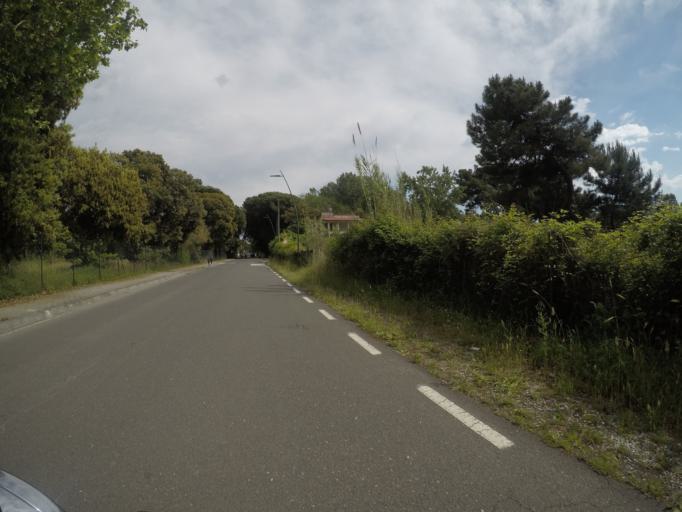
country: IT
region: Tuscany
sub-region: Provincia di Massa-Carrara
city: Capanne-Prato-Cinquale
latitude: 43.9742
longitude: 10.1512
